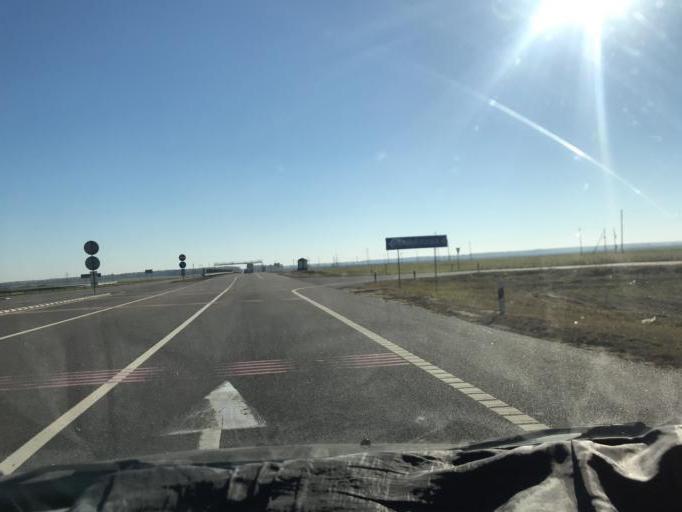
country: BY
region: Mogilev
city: Yalizava
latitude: 53.2348
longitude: 28.9749
